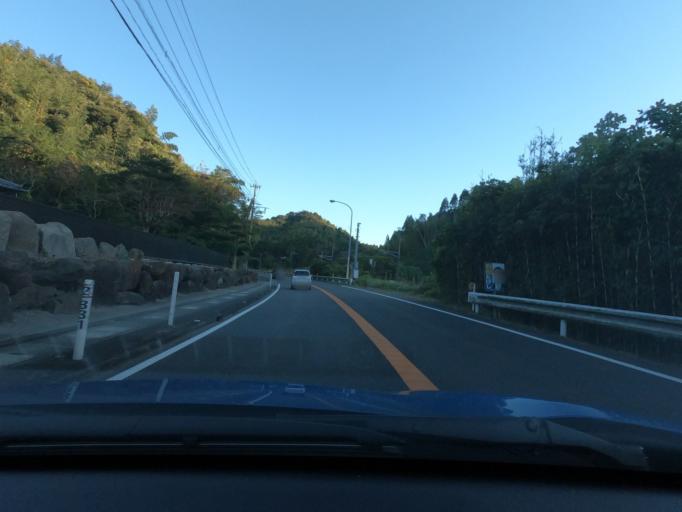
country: JP
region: Kagoshima
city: Satsumasendai
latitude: 31.8522
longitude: 130.2365
